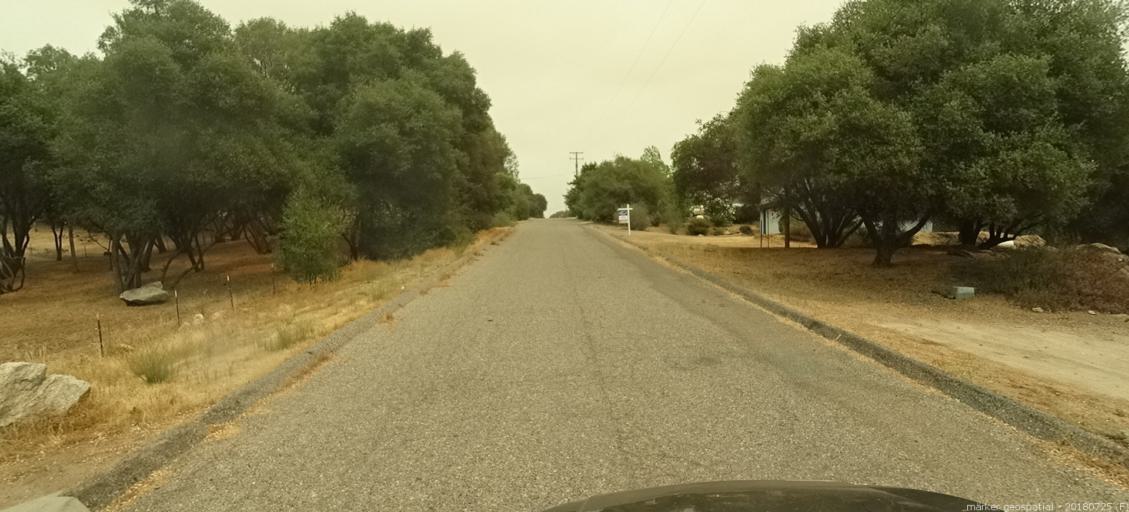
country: US
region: California
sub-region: Madera County
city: Coarsegold
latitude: 37.2189
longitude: -119.6886
